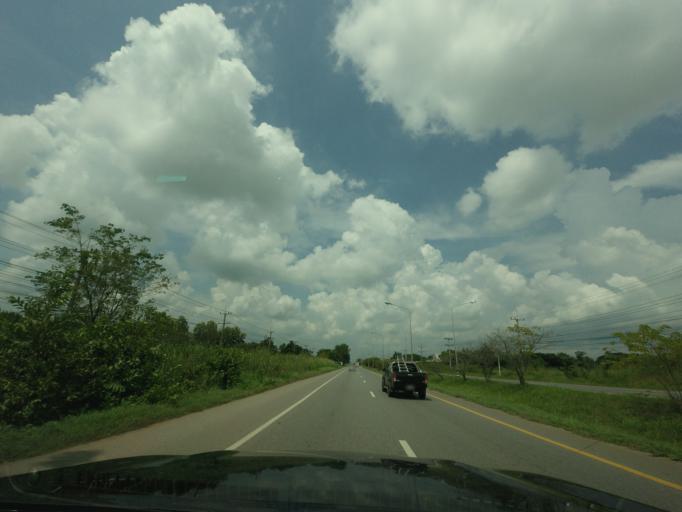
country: TH
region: Khon Kaen
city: Nong Ruea
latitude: 16.4891
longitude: 102.4540
